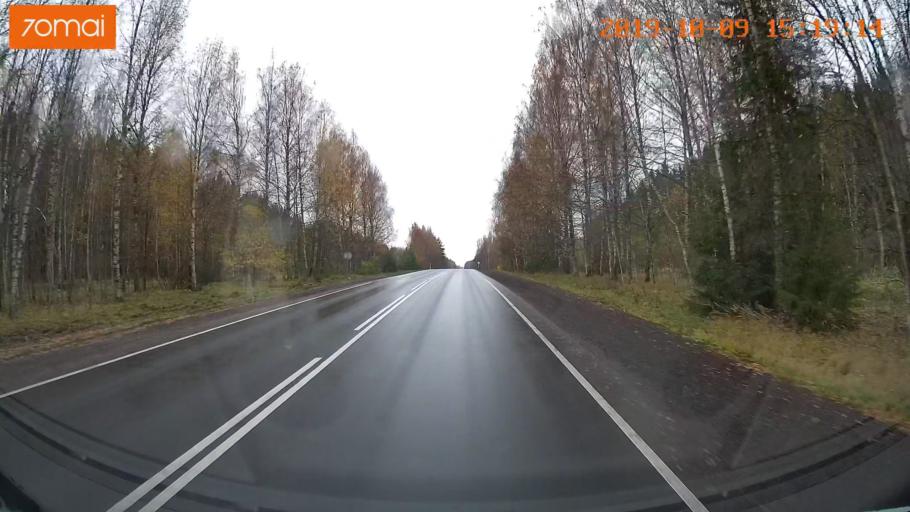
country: RU
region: Kostroma
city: Susanino
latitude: 58.0779
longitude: 41.5600
